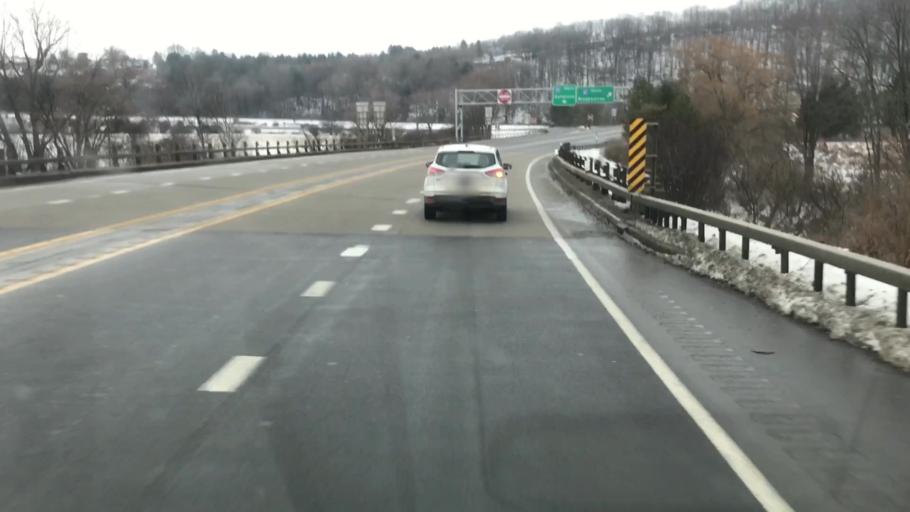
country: US
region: New York
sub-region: Cortland County
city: Homer
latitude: 42.6276
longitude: -76.1807
